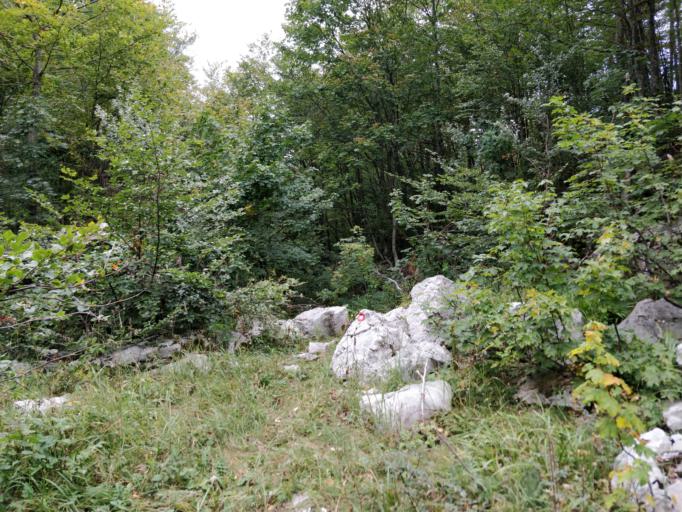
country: HR
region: Zadarska
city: Starigrad
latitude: 44.3756
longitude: 15.5025
